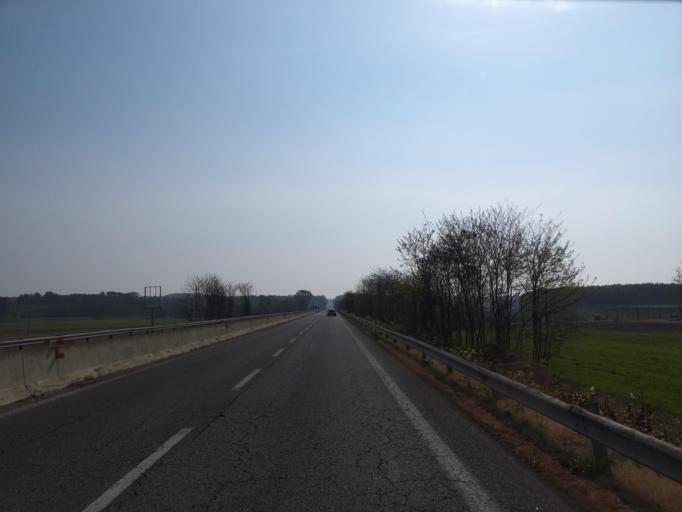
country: IT
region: Piedmont
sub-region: Provincia di Biella
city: Cossato
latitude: 45.5525
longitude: 8.1802
